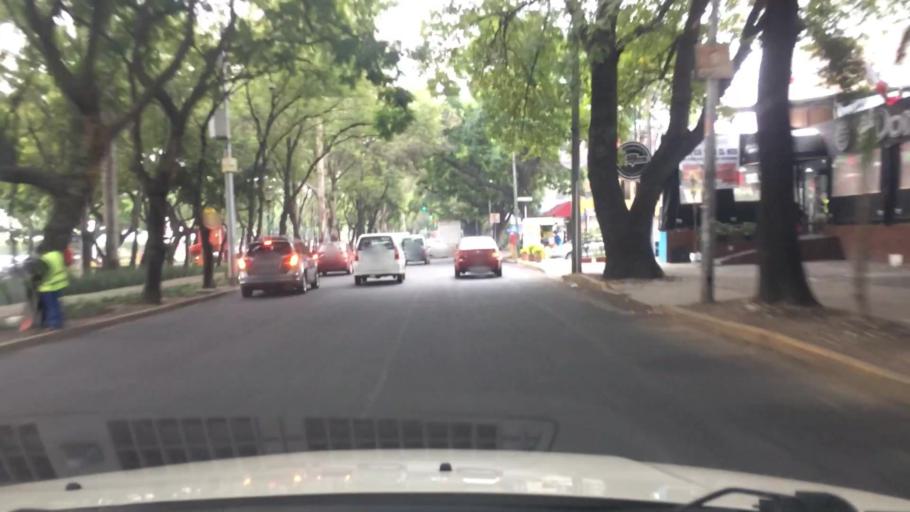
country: MX
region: Mexico City
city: Coyoacan
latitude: 19.3209
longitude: -99.1329
